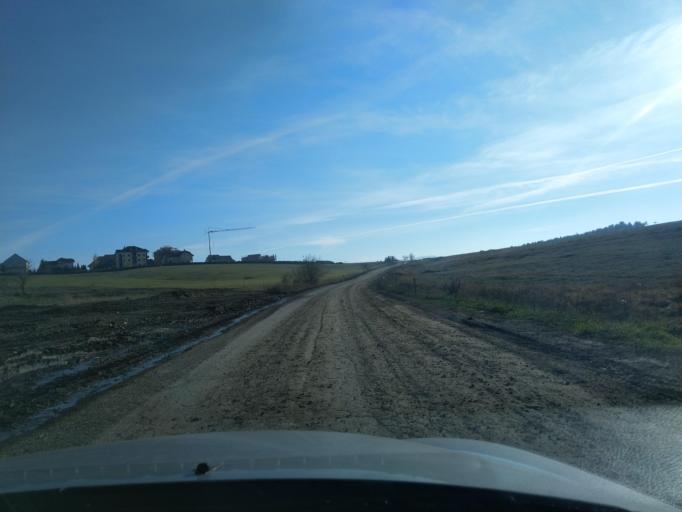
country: RS
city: Zlatibor
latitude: 43.7301
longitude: 19.6820
